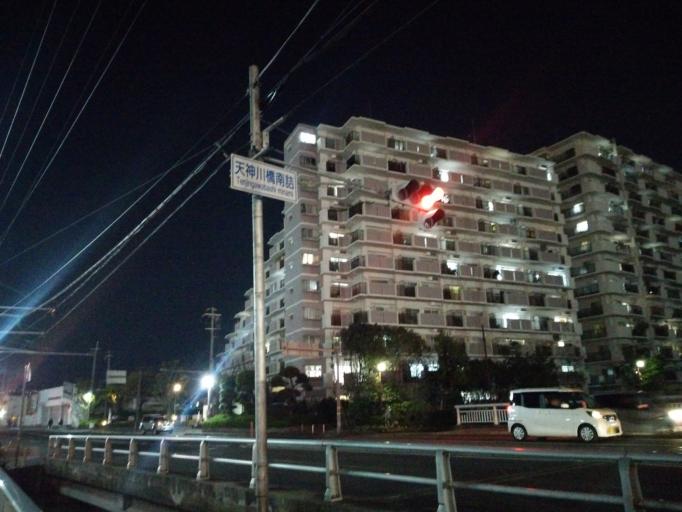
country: JP
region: Hyogo
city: Itami
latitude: 34.7869
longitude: 135.3828
